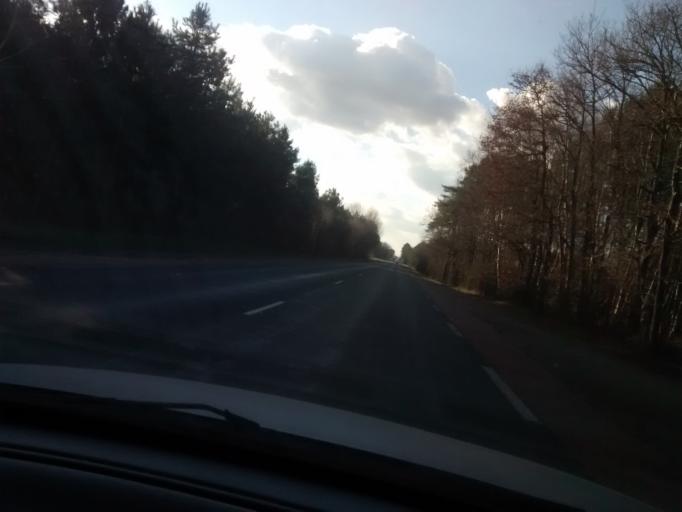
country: FR
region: Pays de la Loire
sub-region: Departement de la Sarthe
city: Champagne
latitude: 48.0066
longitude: 0.3512
